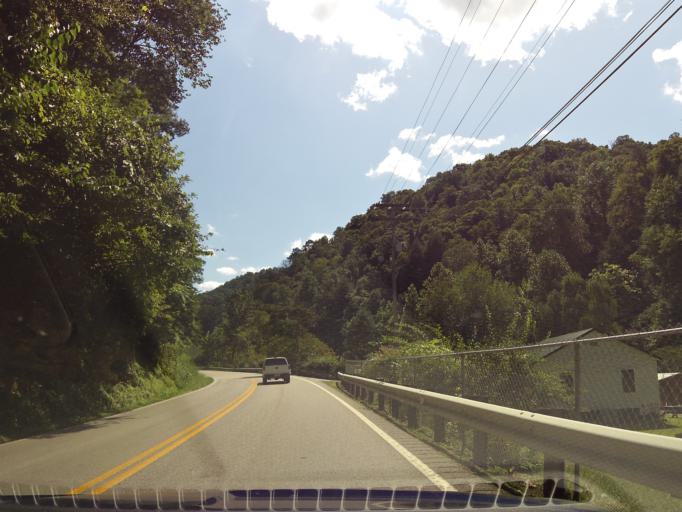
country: US
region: Kentucky
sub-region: Leslie County
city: Hyden
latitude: 37.0306
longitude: -83.3933
